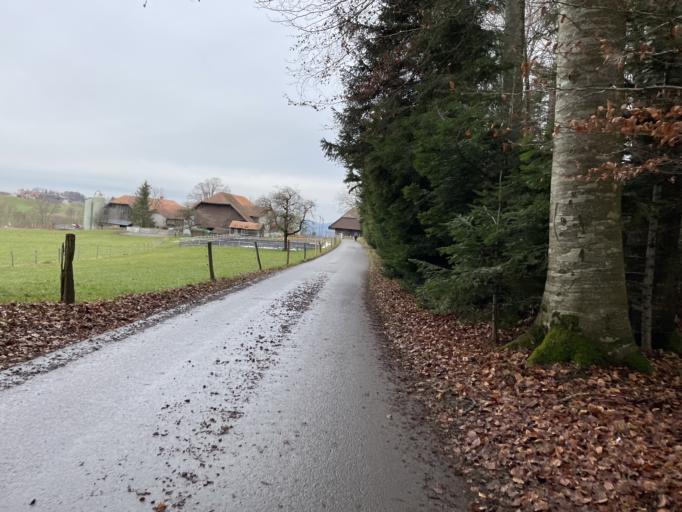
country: CH
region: Bern
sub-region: Bern-Mittelland District
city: Munsingen
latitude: 46.8588
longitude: 7.5357
